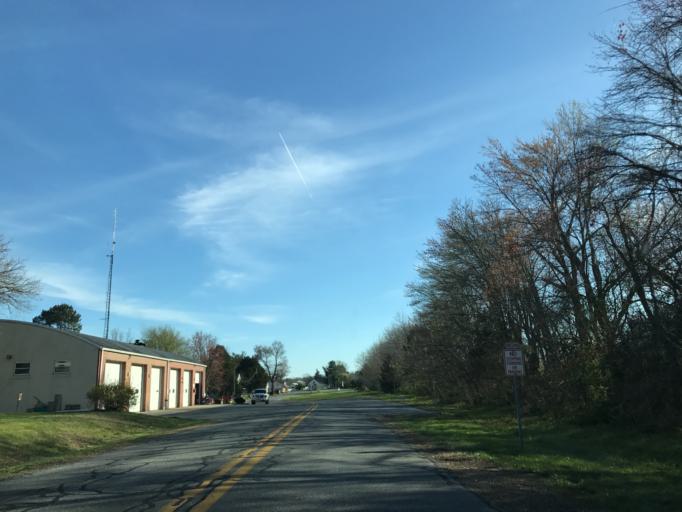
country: US
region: Maryland
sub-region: Caroline County
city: Greensboro
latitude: 39.1148
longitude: -75.7449
